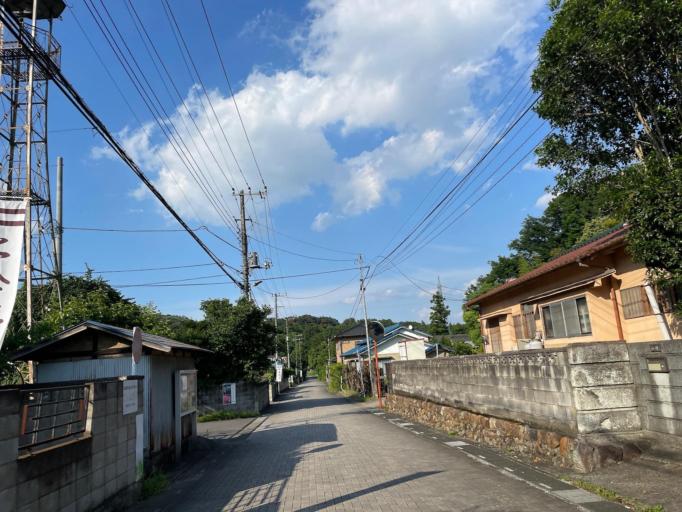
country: JP
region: Saitama
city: Sakado
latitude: 36.0045
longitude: 139.3670
